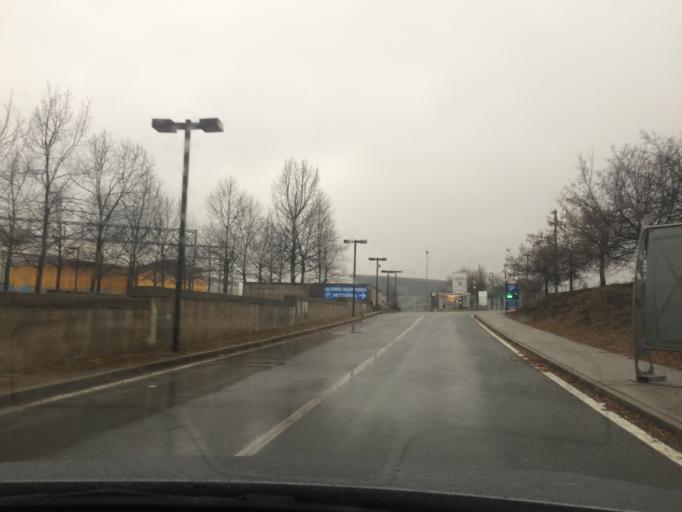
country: IT
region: Piedmont
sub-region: Provincia di Torino
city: Moncalieri
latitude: 45.0310
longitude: 7.6624
